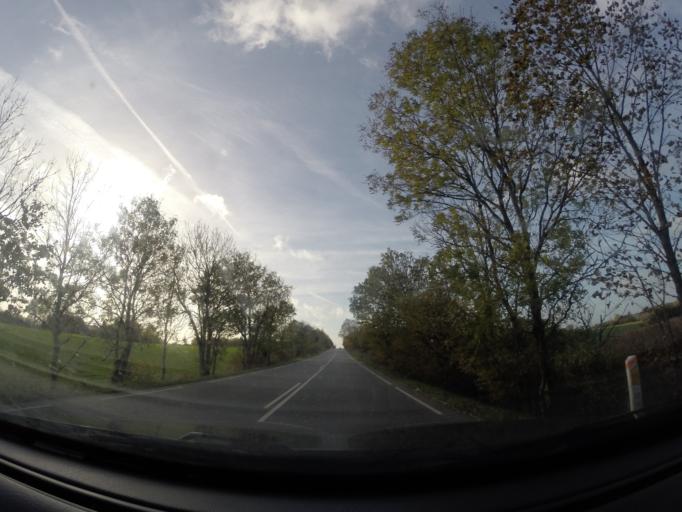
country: DK
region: South Denmark
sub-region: Faaborg-Midtfyn Kommune
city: Ringe
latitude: 55.1999
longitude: 10.5582
